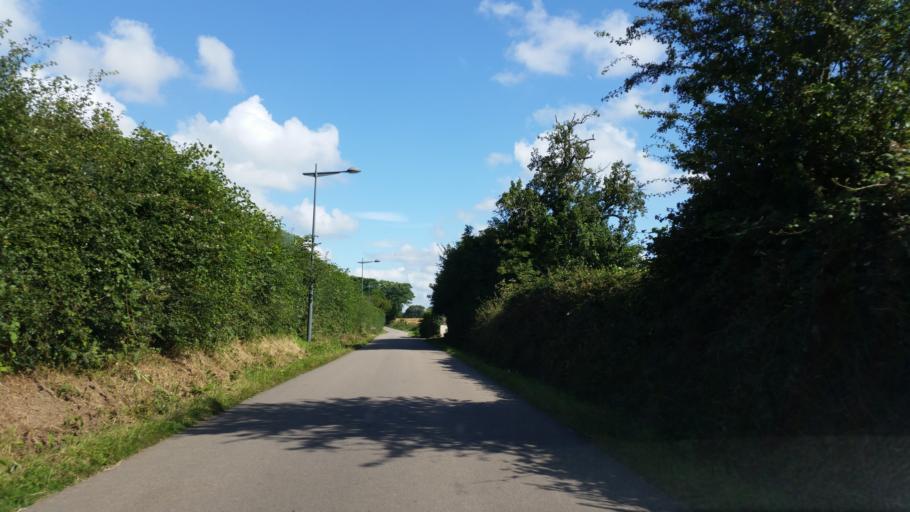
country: FR
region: Lower Normandy
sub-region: Departement du Calvados
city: Amfreville
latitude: 49.2492
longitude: -0.2278
